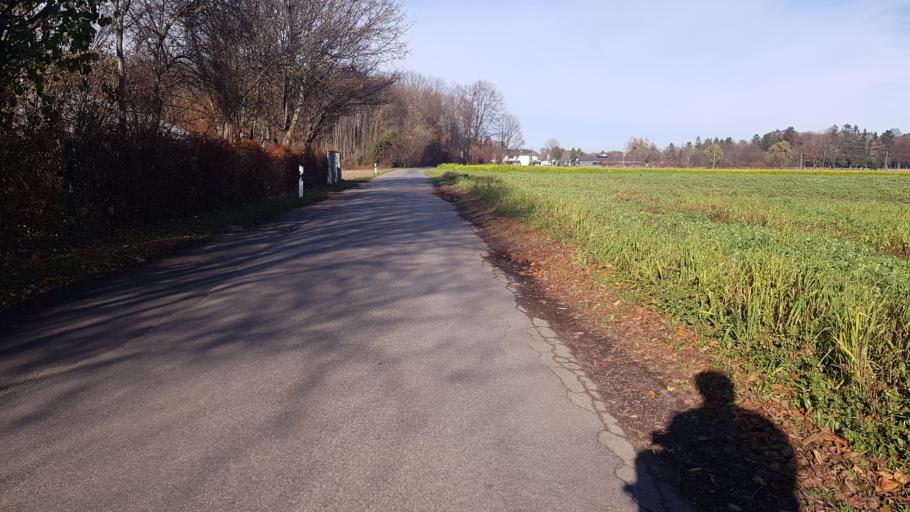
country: DE
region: Bavaria
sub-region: Upper Bavaria
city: Karlsfeld
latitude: 48.2117
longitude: 11.5220
